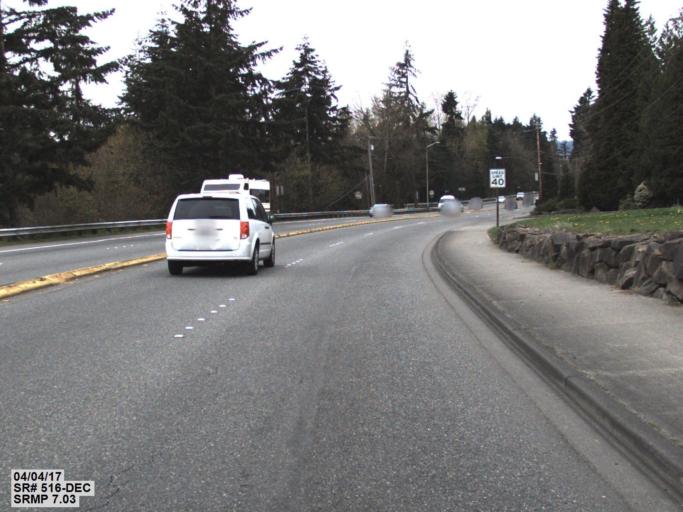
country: US
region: Washington
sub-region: King County
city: Kent
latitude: 47.3731
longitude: -122.2089
